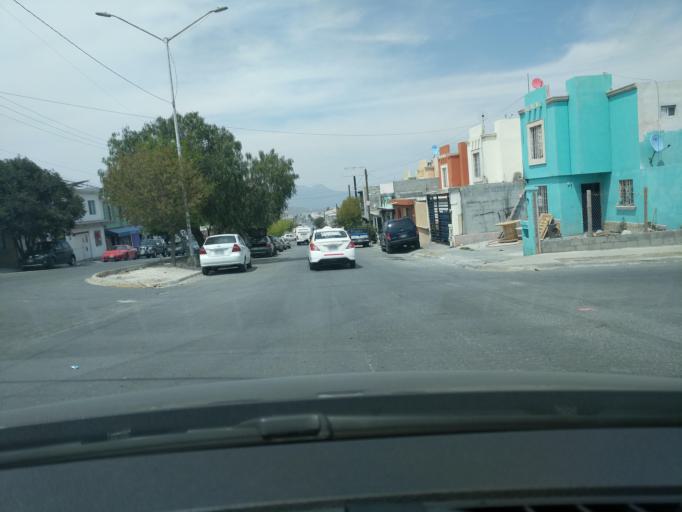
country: MX
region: Coahuila
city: Saltillo
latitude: 25.3505
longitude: -101.0113
